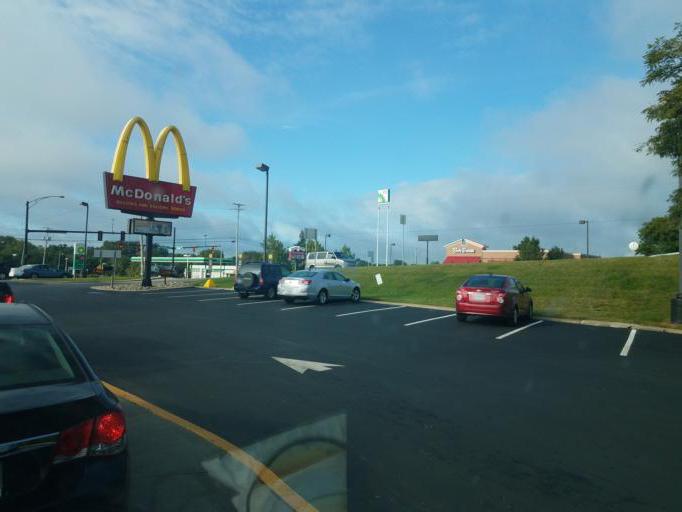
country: US
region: Ohio
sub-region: Richland County
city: Mansfield
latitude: 40.7737
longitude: -82.5512
